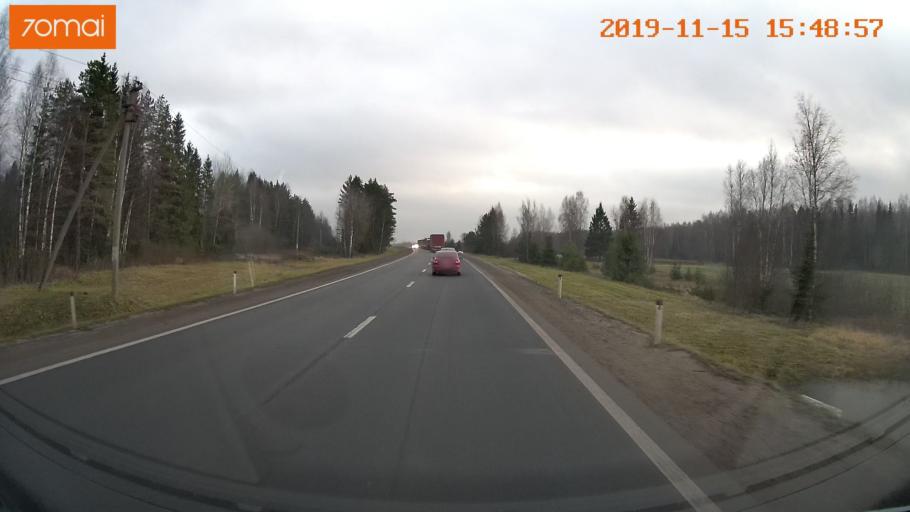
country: RU
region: Jaroslavl
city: Danilov
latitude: 57.9217
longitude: 40.0067
